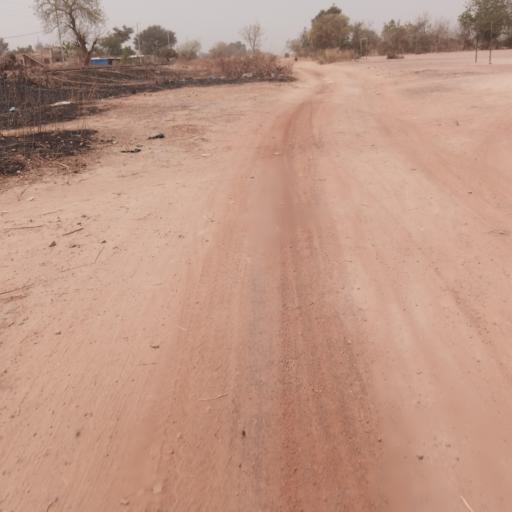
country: BF
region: Centre
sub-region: Kadiogo Province
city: Ouagadougou
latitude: 12.3438
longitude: -1.6760
